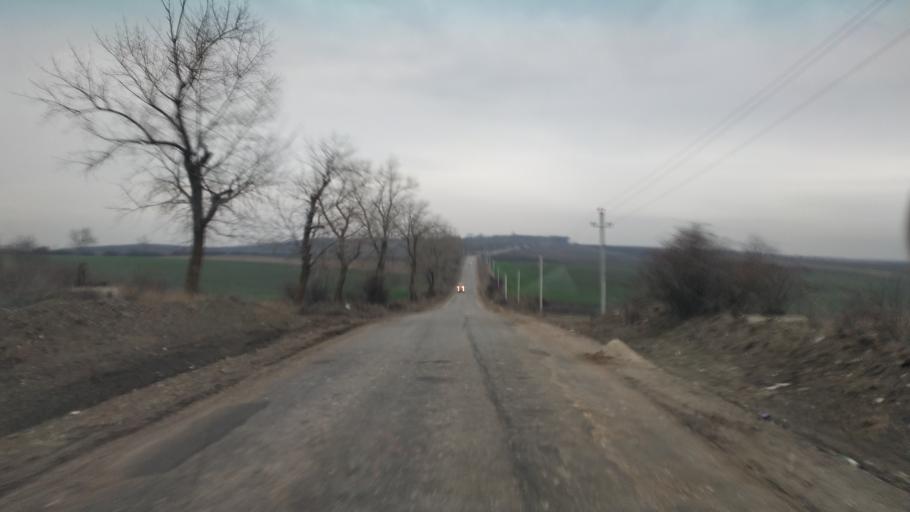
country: MD
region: Chisinau
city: Singera
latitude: 46.8495
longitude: 28.9976
